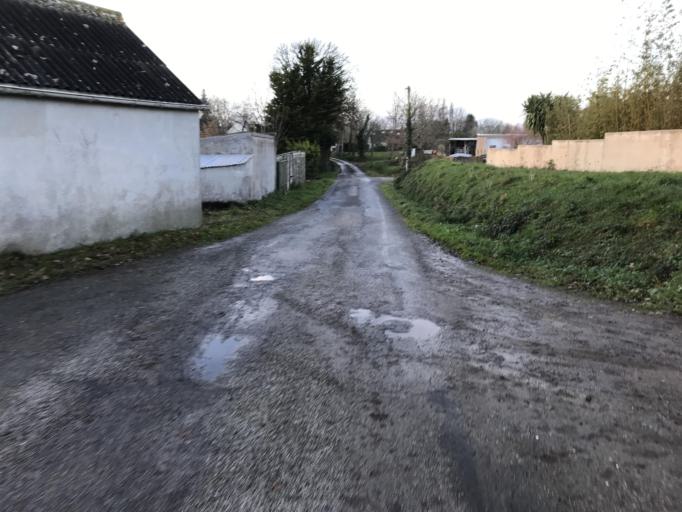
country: FR
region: Brittany
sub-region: Departement du Finistere
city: Hopital-Camfrout
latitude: 48.3345
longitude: -4.2529
